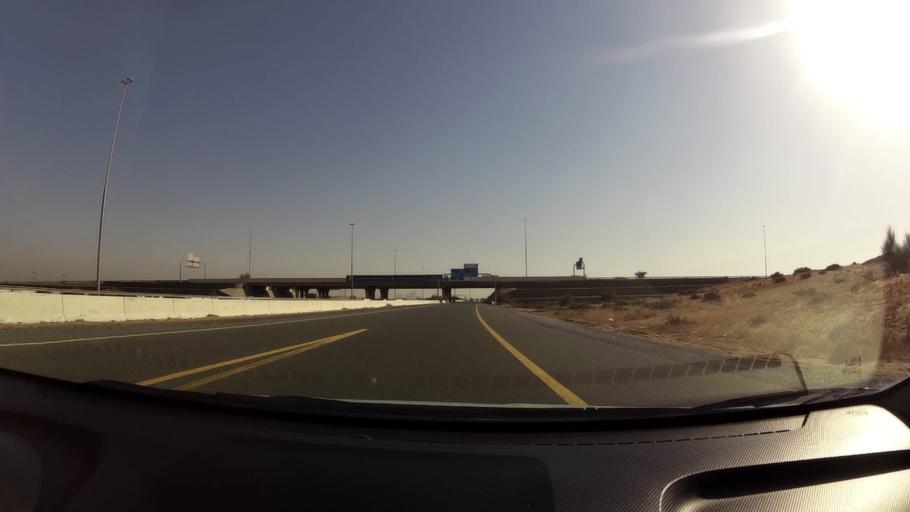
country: AE
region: Umm al Qaywayn
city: Umm al Qaywayn
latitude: 25.4532
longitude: 55.6155
